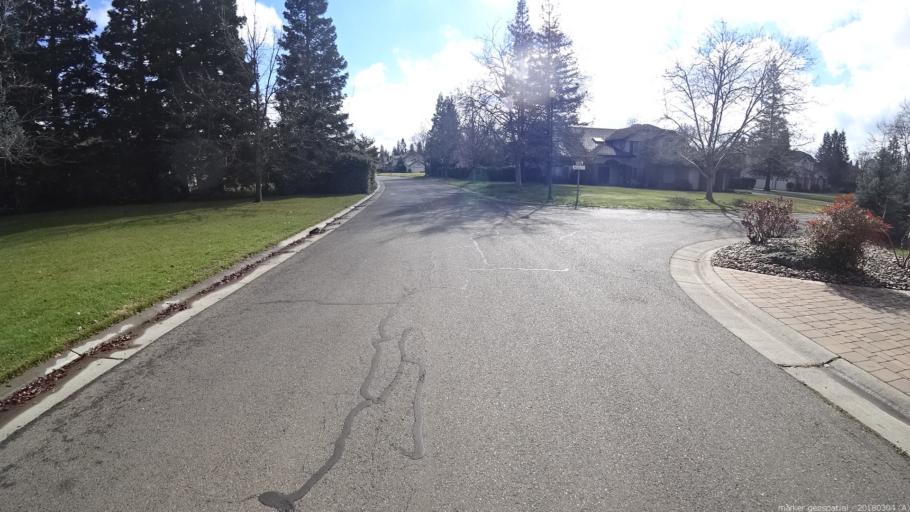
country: US
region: California
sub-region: Sacramento County
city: Vineyard
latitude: 38.4627
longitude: -121.3222
